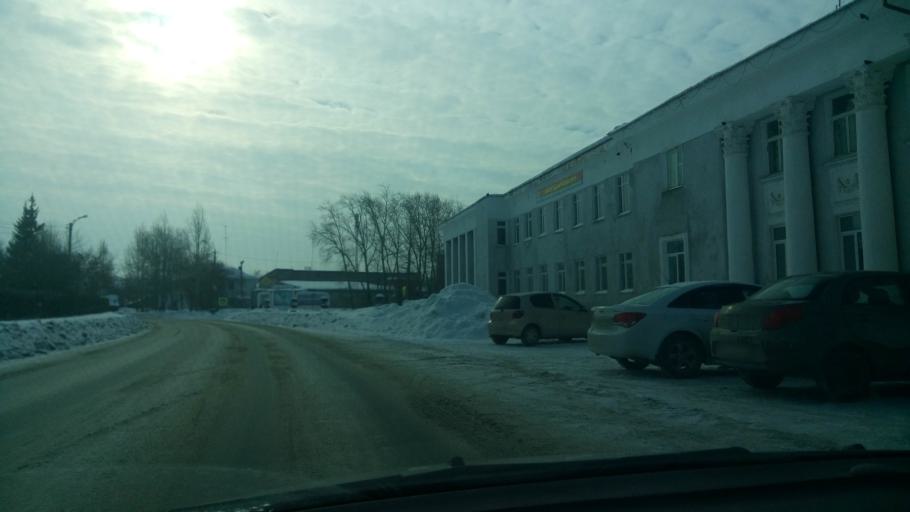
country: RU
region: Sverdlovsk
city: Bogdanovich
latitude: 56.7736
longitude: 62.0554
